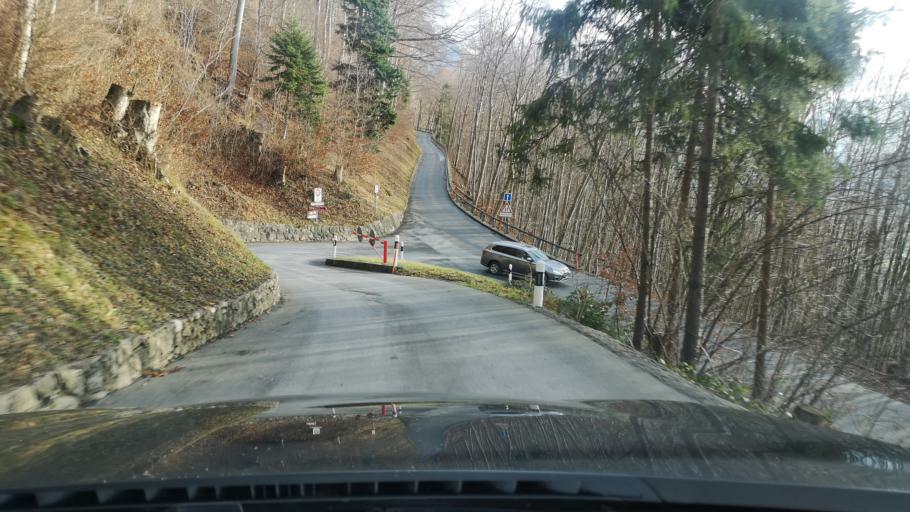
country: LI
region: Vaduz
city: Vaduz
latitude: 47.1295
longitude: 9.5309
